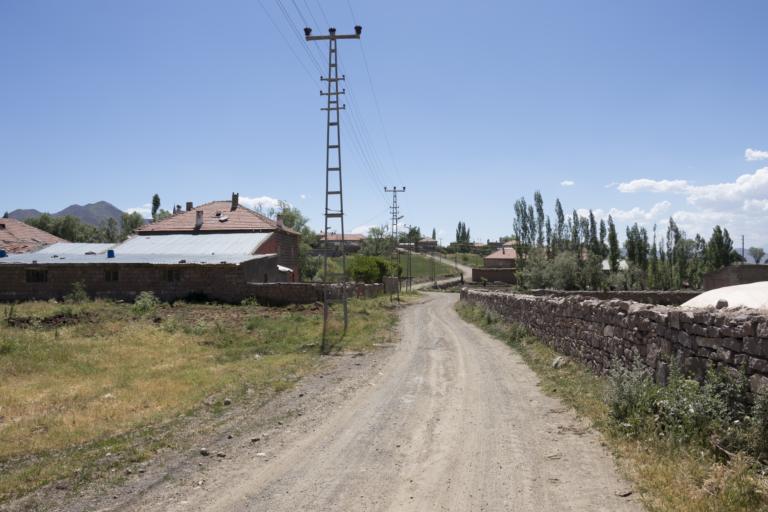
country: TR
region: Kayseri
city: Toklar
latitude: 38.4234
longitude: 36.0977
